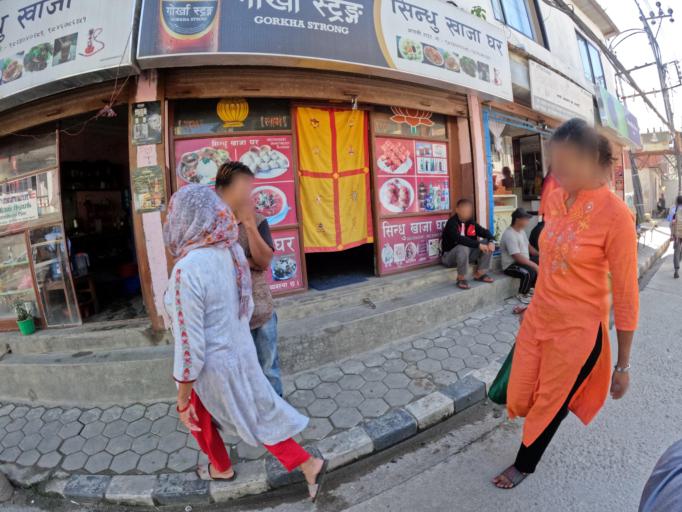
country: NP
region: Central Region
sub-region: Bagmati Zone
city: Kathmandu
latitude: 27.7507
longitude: 85.3365
